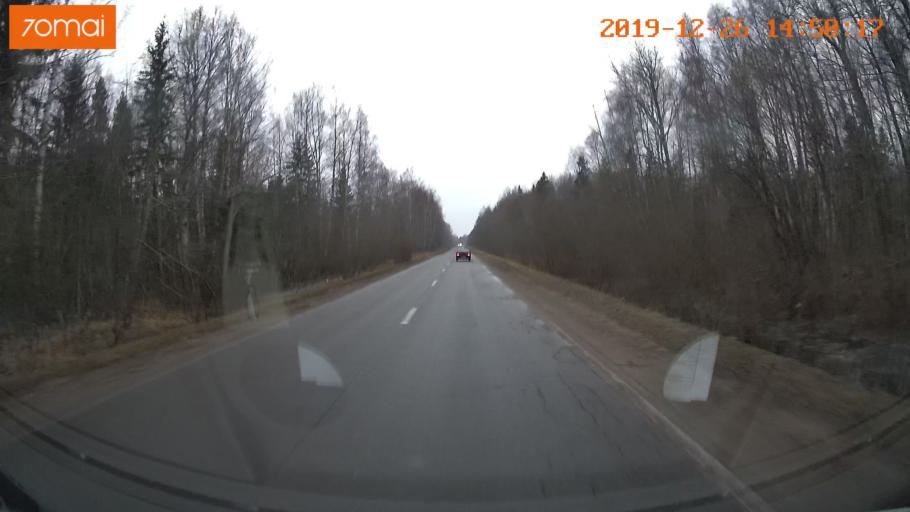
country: RU
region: Jaroslavl
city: Poshekhon'ye
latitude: 58.3331
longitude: 38.9284
